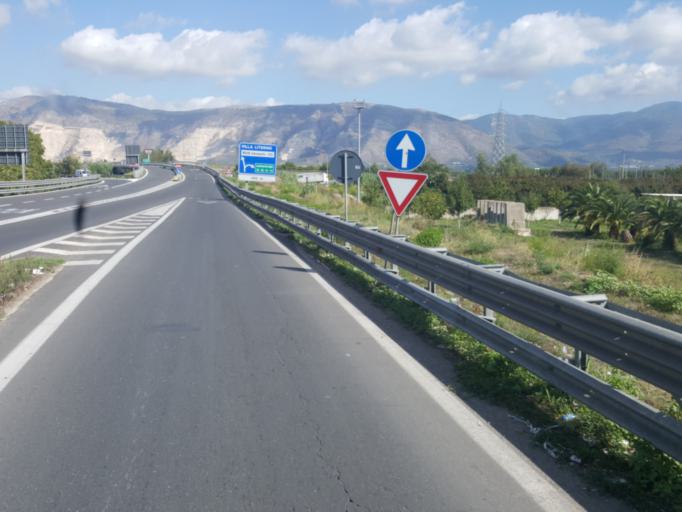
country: IT
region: Campania
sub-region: Provincia di Napoli
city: Cimitile
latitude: 40.9343
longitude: 14.4998
